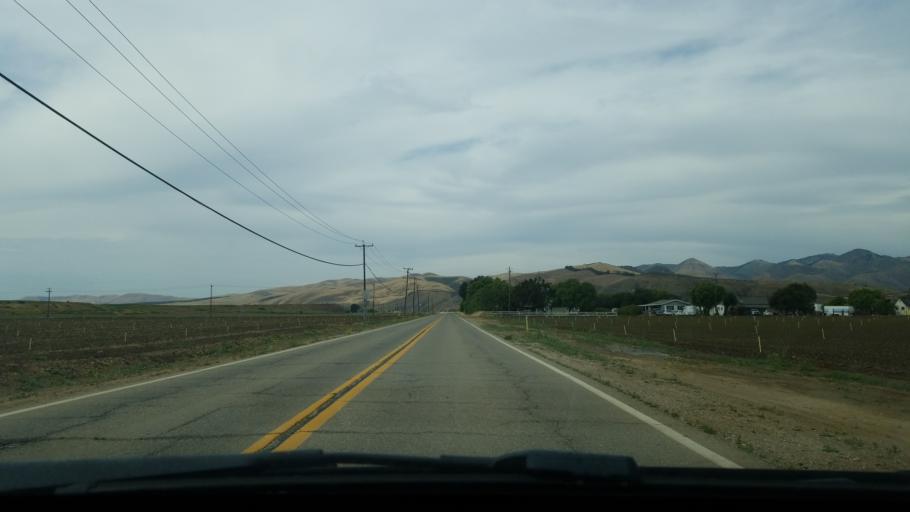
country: US
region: California
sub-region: Santa Barbara County
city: Orcutt
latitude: 34.8913
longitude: -120.3150
